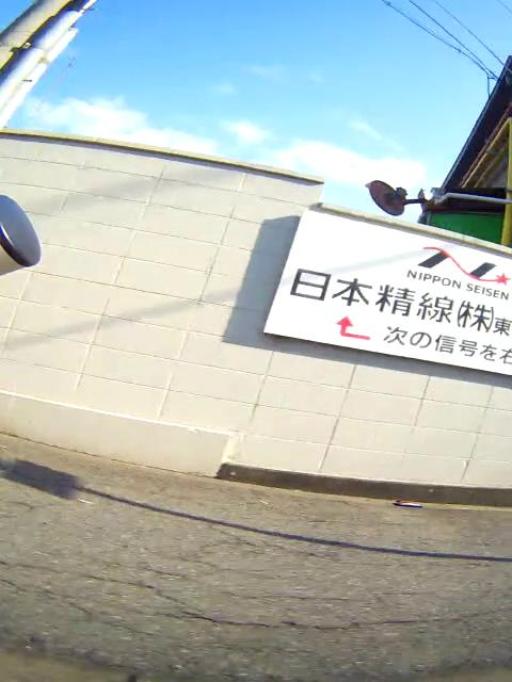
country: JP
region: Osaka
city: Daitocho
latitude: 34.6988
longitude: 135.5884
